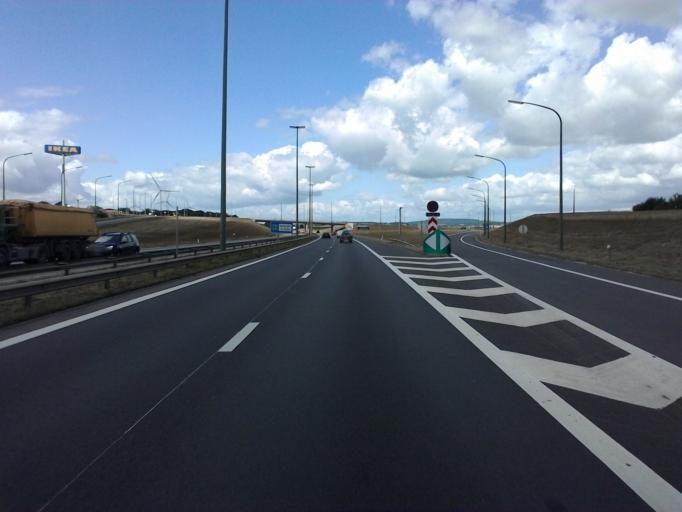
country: LU
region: Luxembourg
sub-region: Canton de Capellen
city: Steinfort
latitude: 49.6400
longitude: 5.8932
